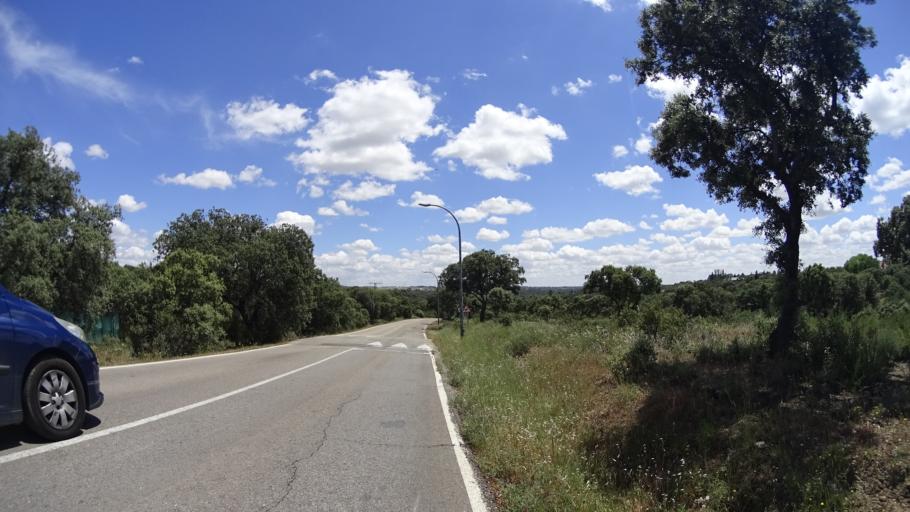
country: ES
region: Madrid
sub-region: Provincia de Madrid
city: Brunete
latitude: 40.4204
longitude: -3.9641
